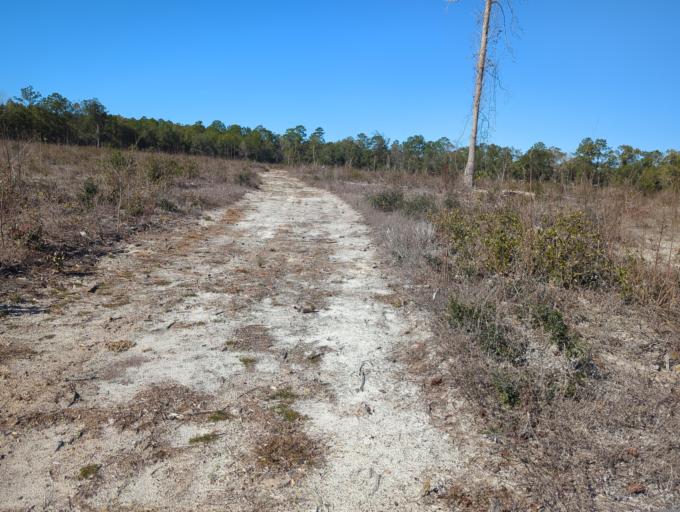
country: US
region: Florida
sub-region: Wakulla County
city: Crawfordville
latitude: 30.1842
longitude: -84.3334
